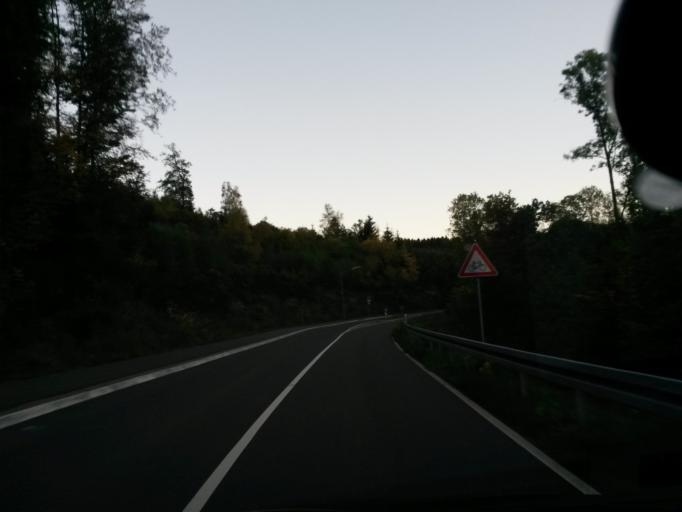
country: DE
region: North Rhine-Westphalia
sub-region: Regierungsbezirk Koln
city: Engelskirchen
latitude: 51.0053
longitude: 7.4689
